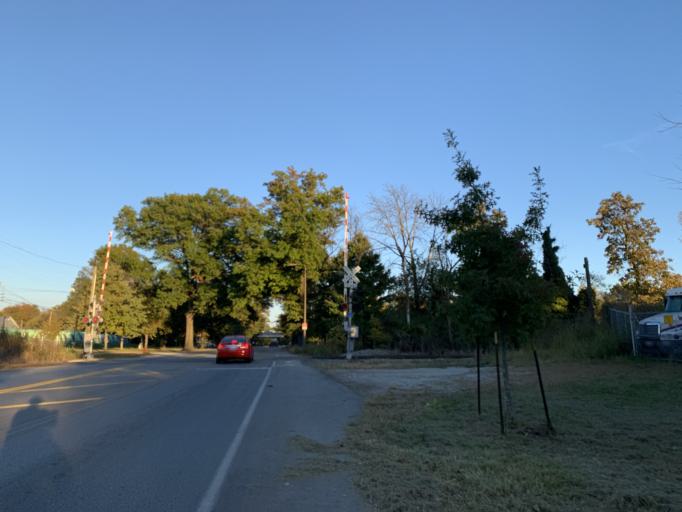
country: US
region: Kentucky
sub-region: Jefferson County
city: Shively
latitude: 38.2260
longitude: -85.8253
